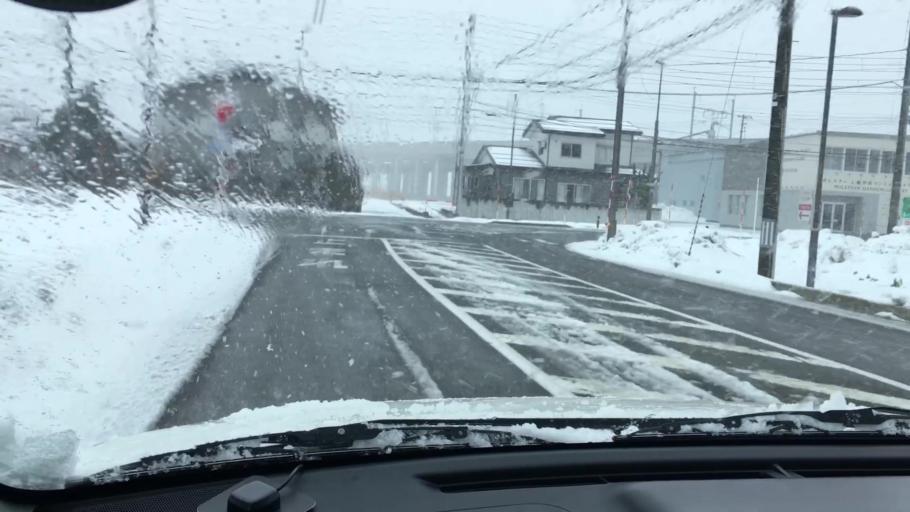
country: JP
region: Niigata
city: Joetsu
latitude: 37.0826
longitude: 138.2448
